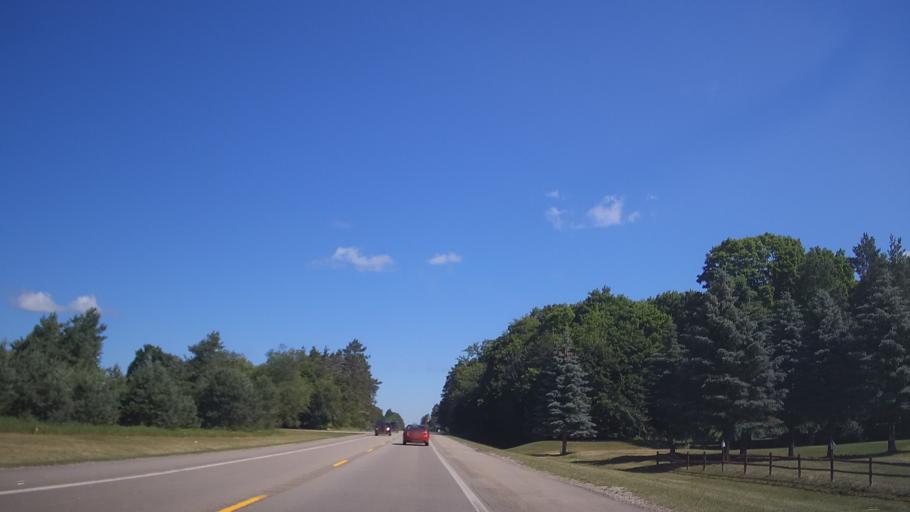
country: US
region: Michigan
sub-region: Cheboygan County
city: Indian River
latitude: 45.5014
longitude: -84.7812
